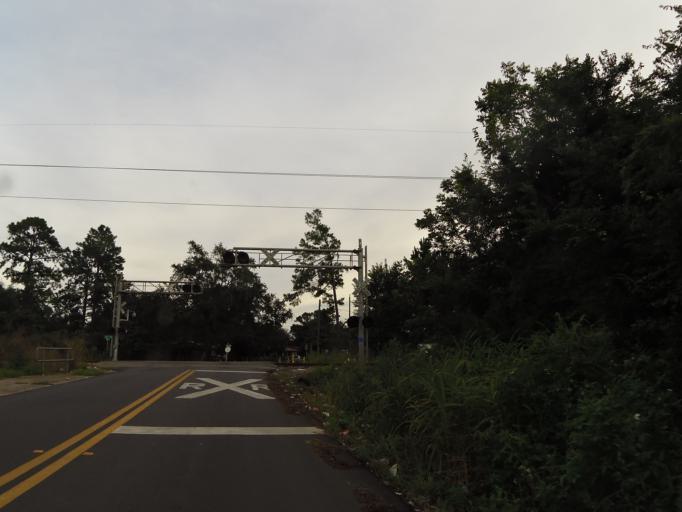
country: US
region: Florida
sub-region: Duval County
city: Jacksonville
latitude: 30.3626
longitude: -81.7087
